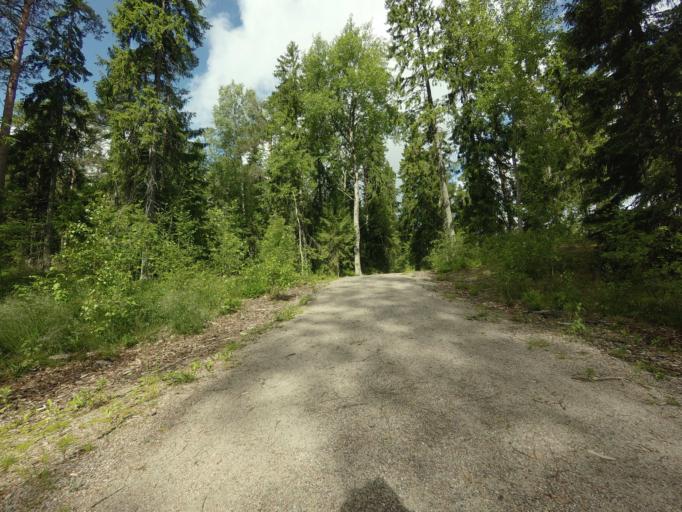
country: FI
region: Uusimaa
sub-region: Helsinki
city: Espoo
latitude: 60.1679
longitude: 24.6052
